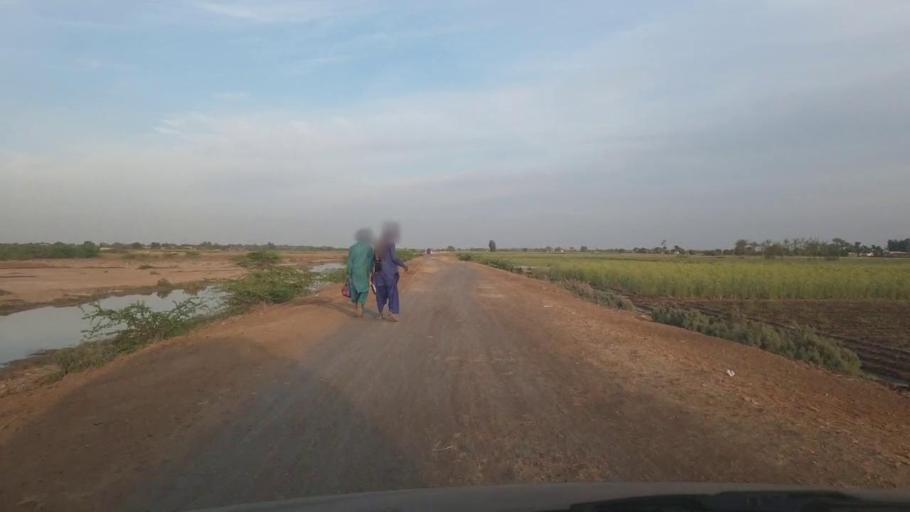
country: PK
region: Sindh
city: Kunri
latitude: 25.2269
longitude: 69.5521
